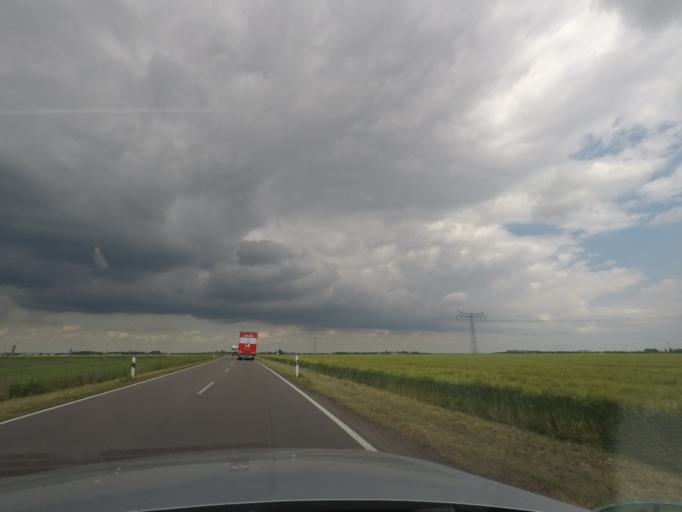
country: DE
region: Saxony
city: Markranstadt
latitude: 51.3317
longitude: 12.2061
